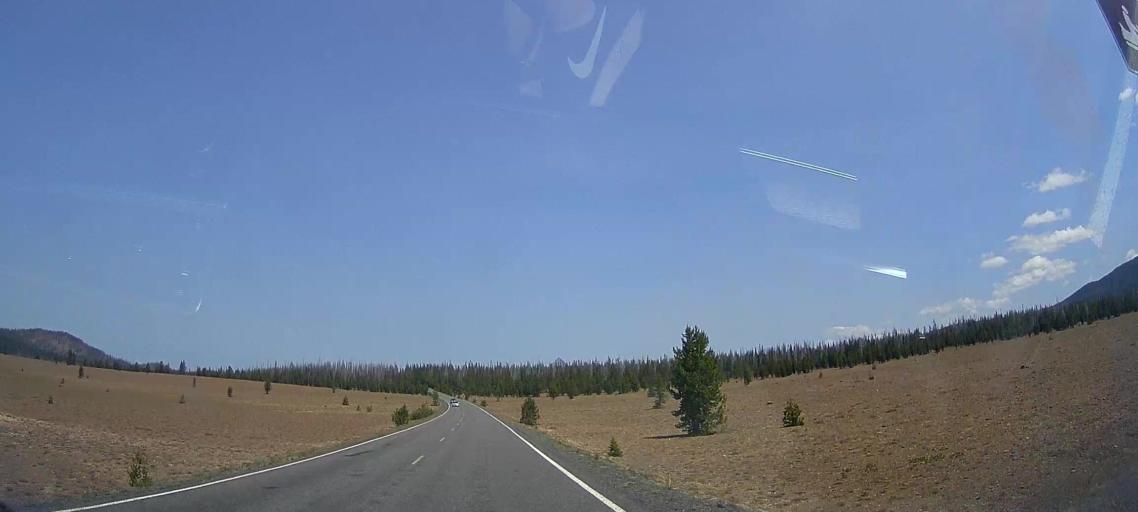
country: US
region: Oregon
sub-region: Lane County
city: Oakridge
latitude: 43.0313
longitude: -122.1179
